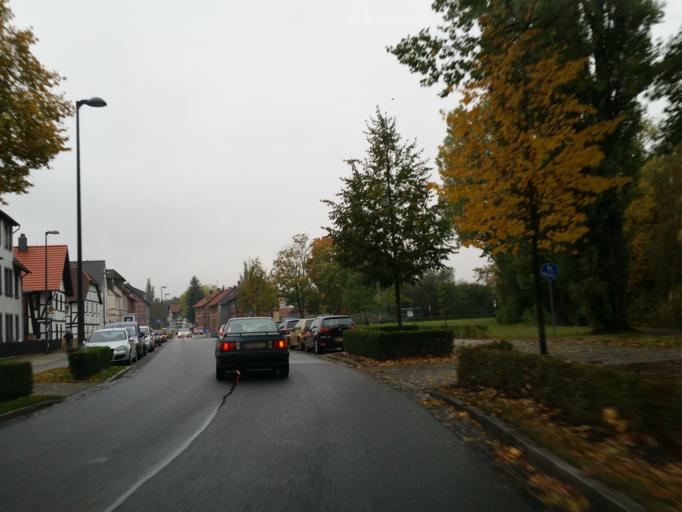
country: DE
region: Lower Saxony
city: Braunschweig
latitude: 52.2703
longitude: 10.5726
